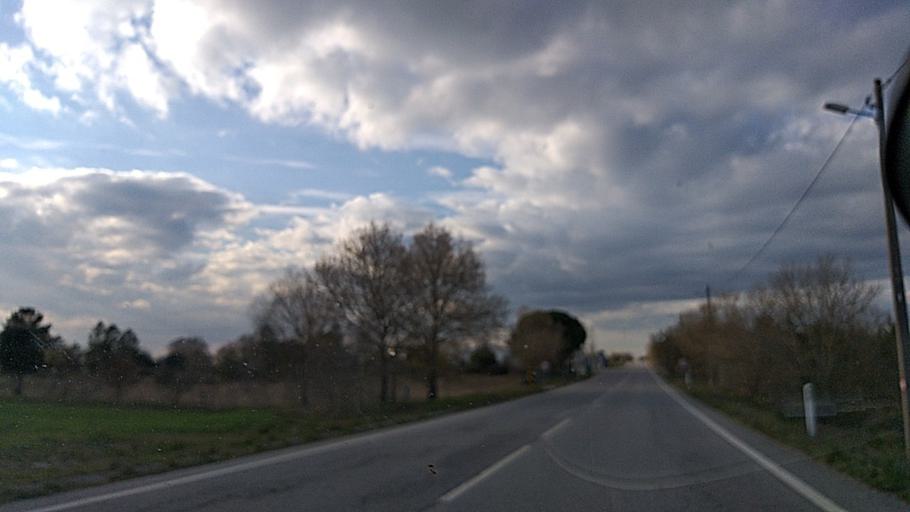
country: ES
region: Castille and Leon
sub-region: Provincia de Salamanca
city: Aldea del Obispo
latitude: 40.7007
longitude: -6.8910
